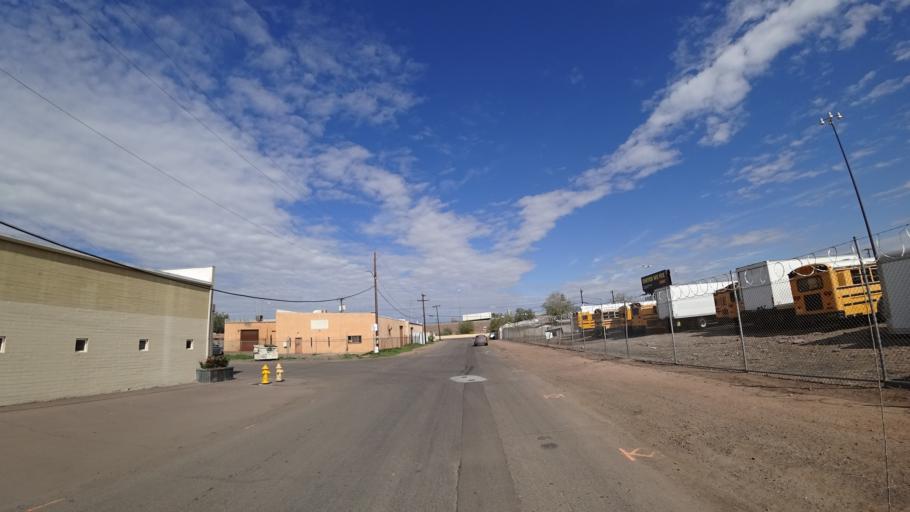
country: US
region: Arizona
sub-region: Maricopa County
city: Phoenix
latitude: 33.4272
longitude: -112.0762
